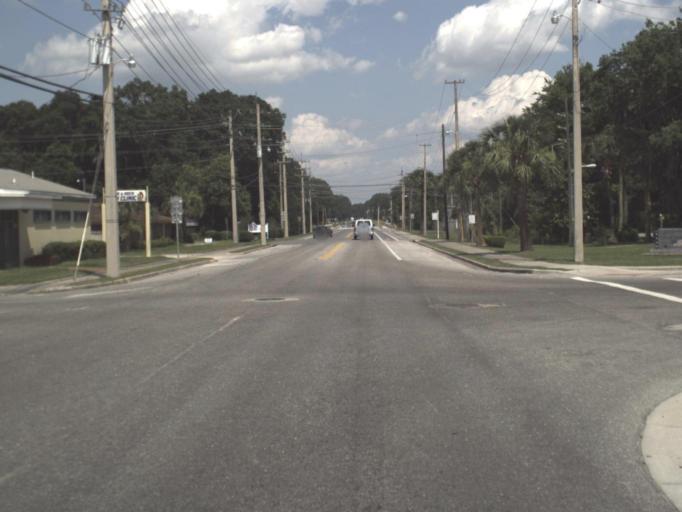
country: US
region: Florida
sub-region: Bradford County
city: Starke
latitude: 29.9432
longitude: -82.1066
